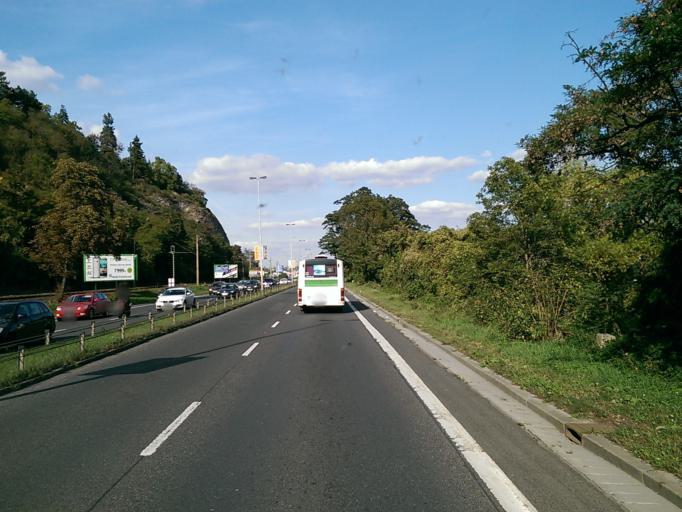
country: CZ
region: Praha
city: Branik
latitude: 50.0322
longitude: 14.4004
